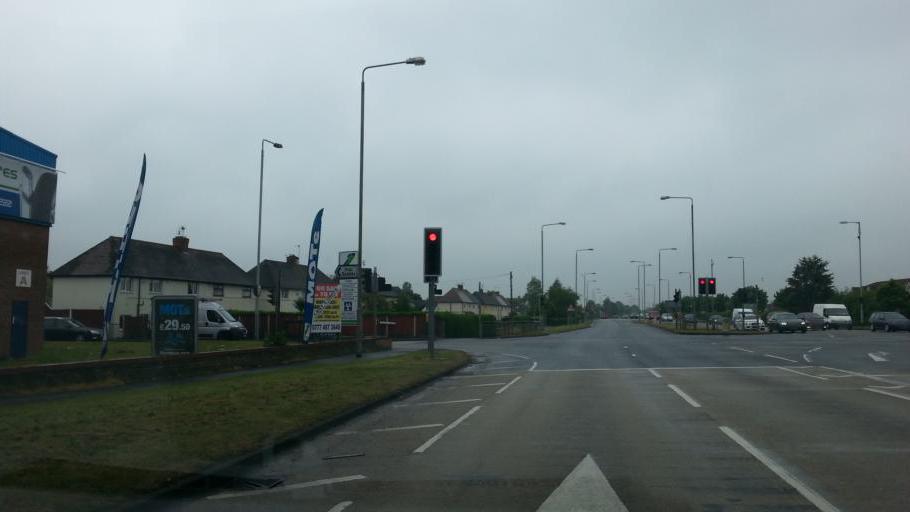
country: GB
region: England
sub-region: Nottinghamshire
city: Newark on Trent
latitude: 53.0918
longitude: -0.7894
